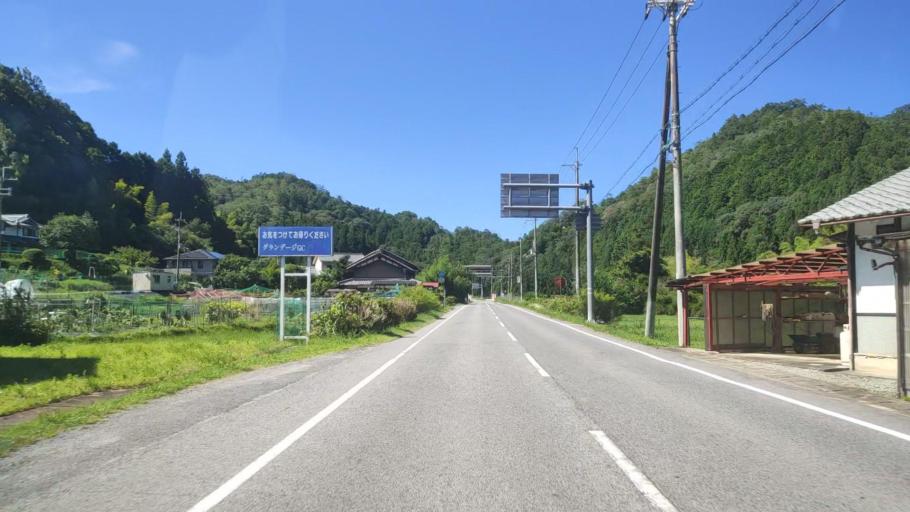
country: JP
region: Nara
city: Yoshino-cho
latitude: 34.4231
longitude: 135.9379
